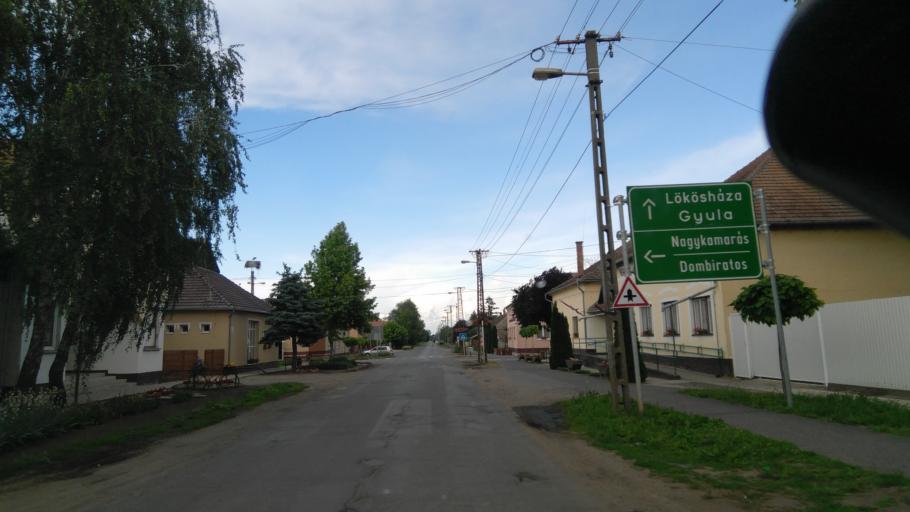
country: HU
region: Bekes
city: Kevermes
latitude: 46.4156
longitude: 21.1804
